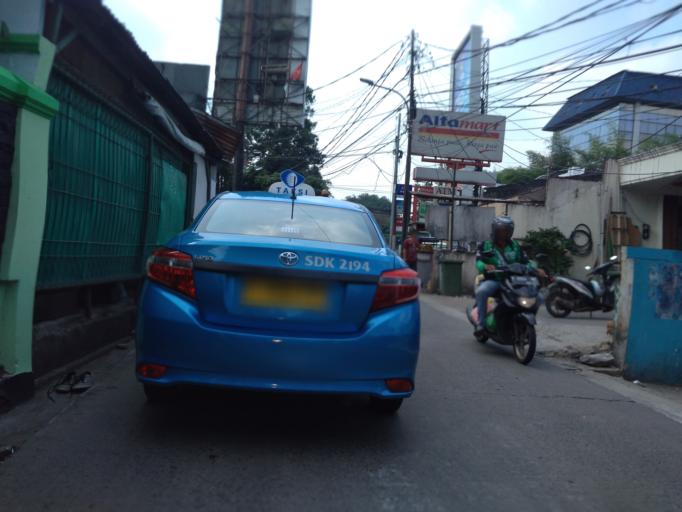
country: ID
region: Jakarta Raya
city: Jakarta
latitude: -6.2729
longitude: 106.8147
